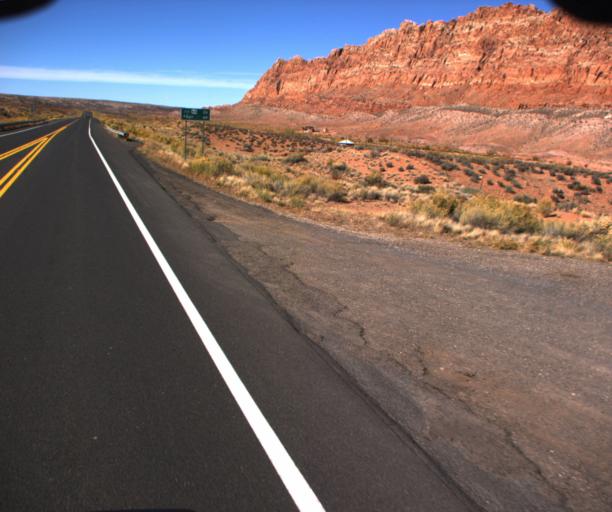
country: US
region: Arizona
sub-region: Coconino County
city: Tuba City
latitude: 36.3052
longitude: -111.4619
